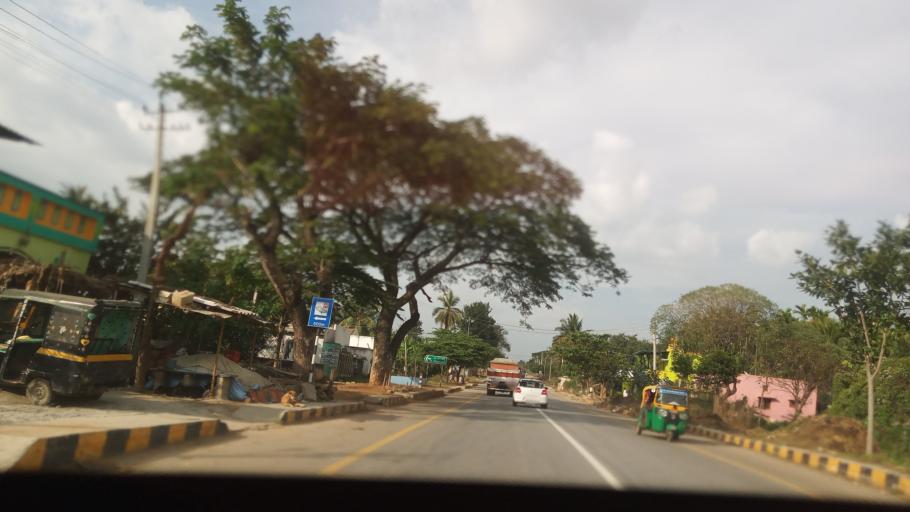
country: IN
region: Karnataka
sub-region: Tumkur
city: Kunigal
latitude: 12.8649
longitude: 77.0400
